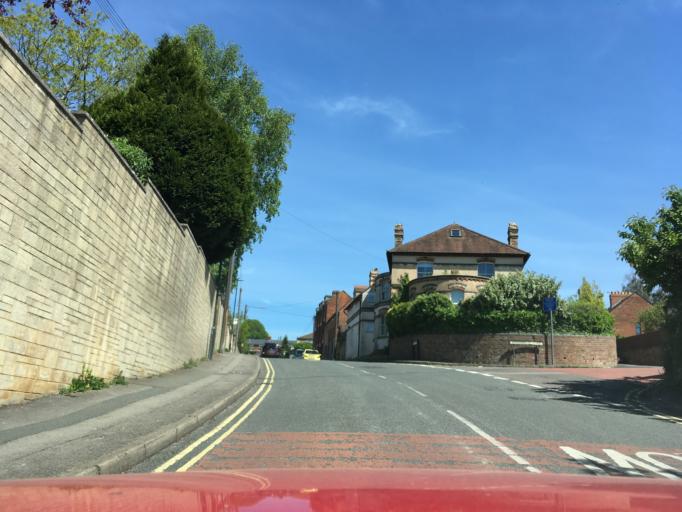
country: GB
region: England
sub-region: Gloucestershire
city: Stroud
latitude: 51.7491
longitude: -2.2141
